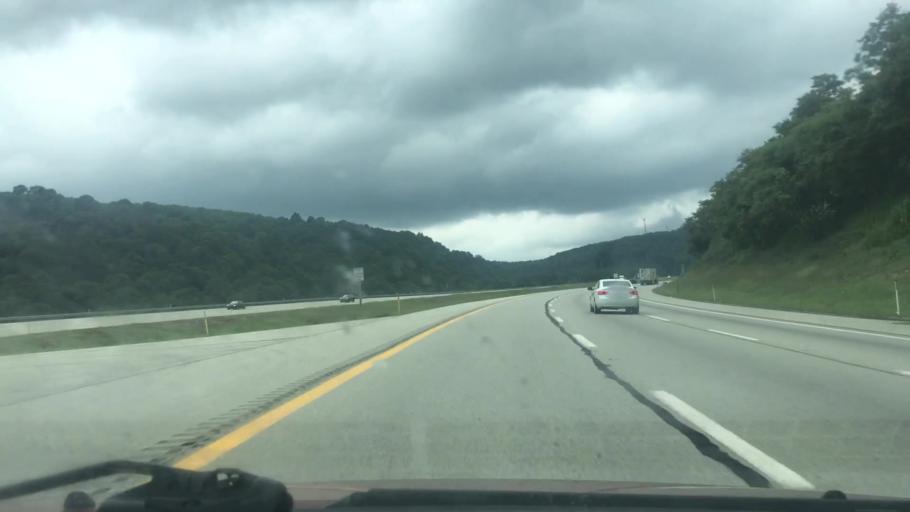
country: US
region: Pennsylvania
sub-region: Somerset County
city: Somerset
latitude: 40.0915
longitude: -79.2021
